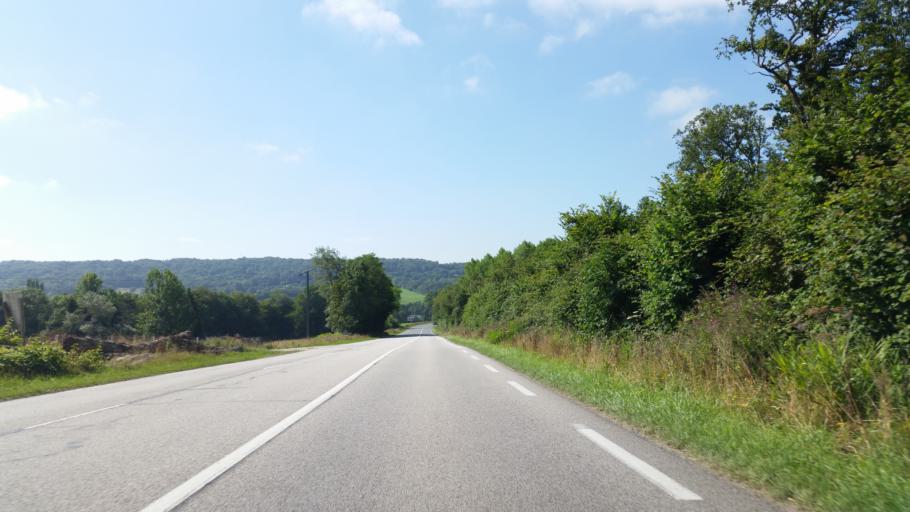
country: FR
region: Lower Normandy
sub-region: Departement du Calvados
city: Saint-Gatien-des-Bois
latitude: 49.3298
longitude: 0.2013
